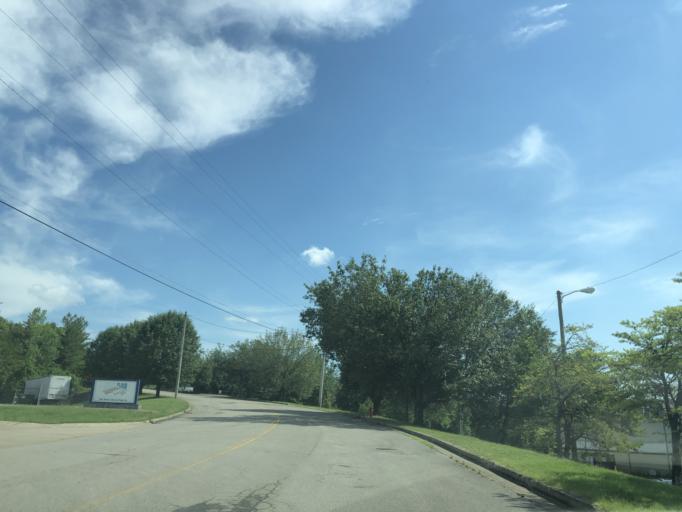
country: US
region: Tennessee
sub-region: Davidson County
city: Nashville
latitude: 36.2258
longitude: -86.7899
